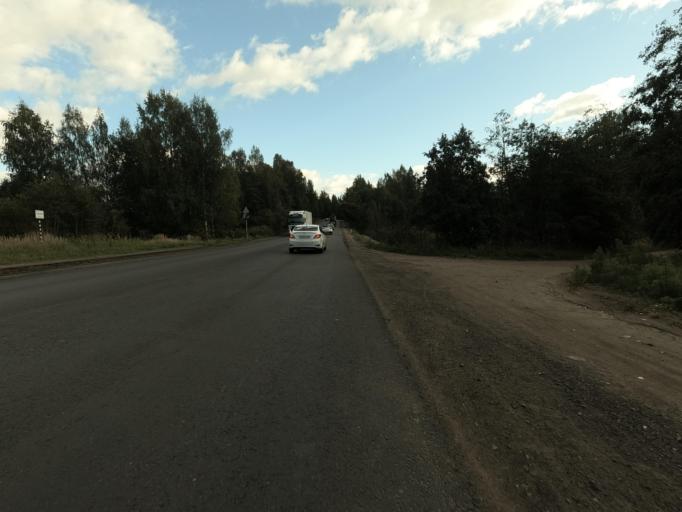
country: RU
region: Leningrad
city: Koltushi
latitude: 59.9684
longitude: 30.6561
